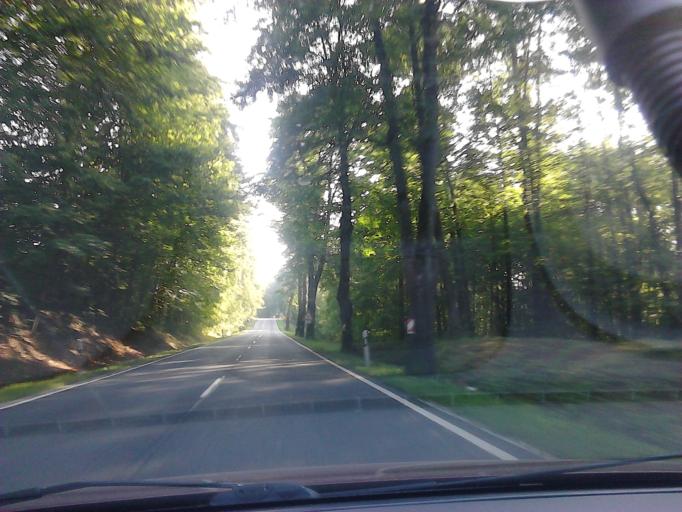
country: DE
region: Bavaria
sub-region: Upper Franconia
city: Weitramsdorf
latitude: 50.2311
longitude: 10.8597
